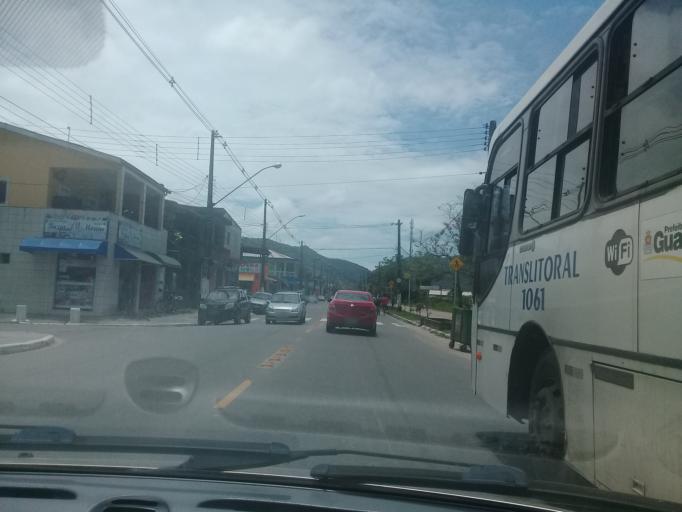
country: BR
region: Sao Paulo
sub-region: Guaruja
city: Guaruja
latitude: -23.9660
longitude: -46.2539
